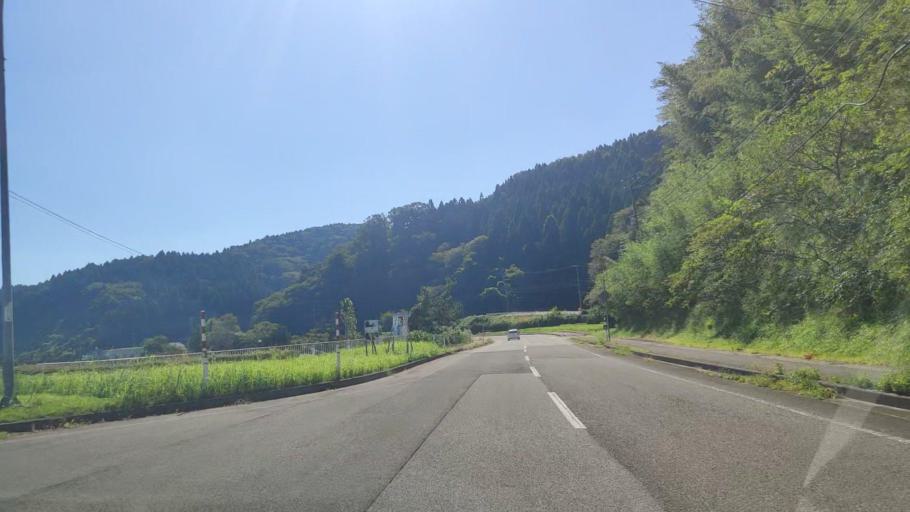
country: JP
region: Ishikawa
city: Nanao
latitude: 37.2897
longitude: 136.7524
